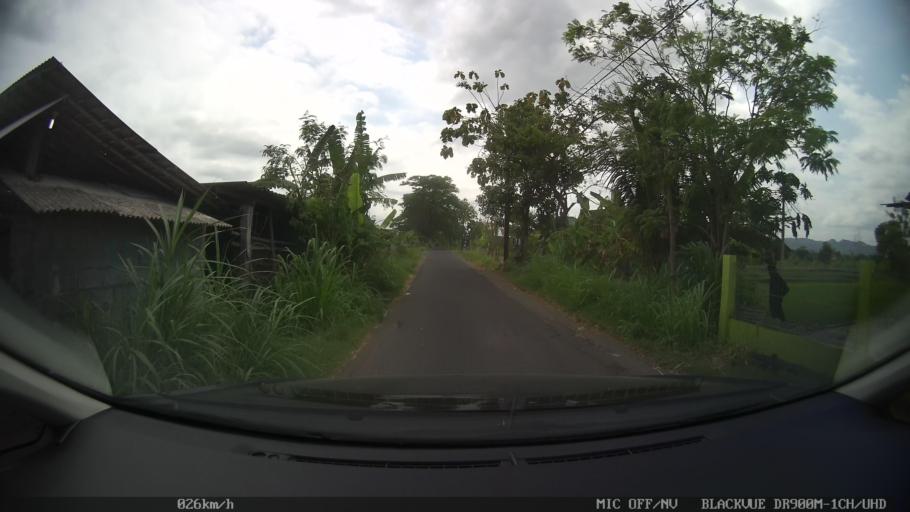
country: ID
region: Daerah Istimewa Yogyakarta
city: Depok
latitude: -7.8281
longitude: 110.4635
